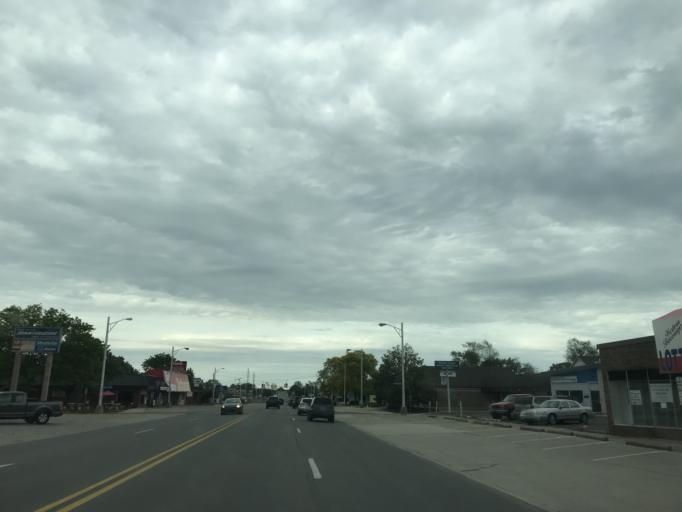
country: US
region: Michigan
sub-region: Wayne County
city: Trenton
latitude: 42.1413
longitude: -83.1957
